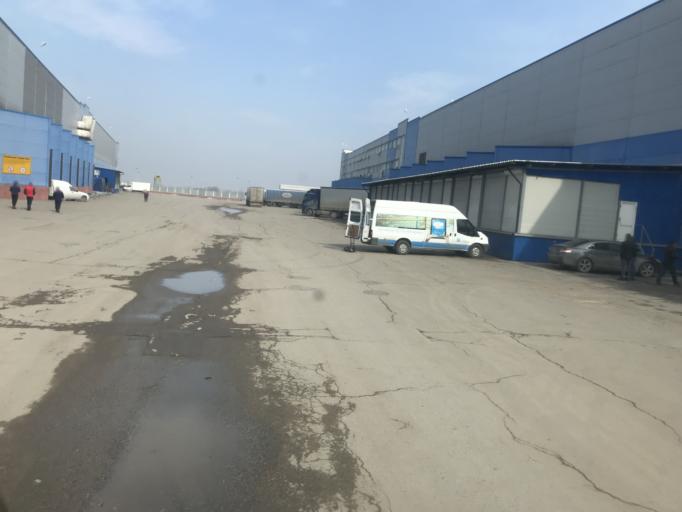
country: KZ
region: Almaty Oblysy
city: Pervomayskiy
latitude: 43.3625
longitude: 76.9766
